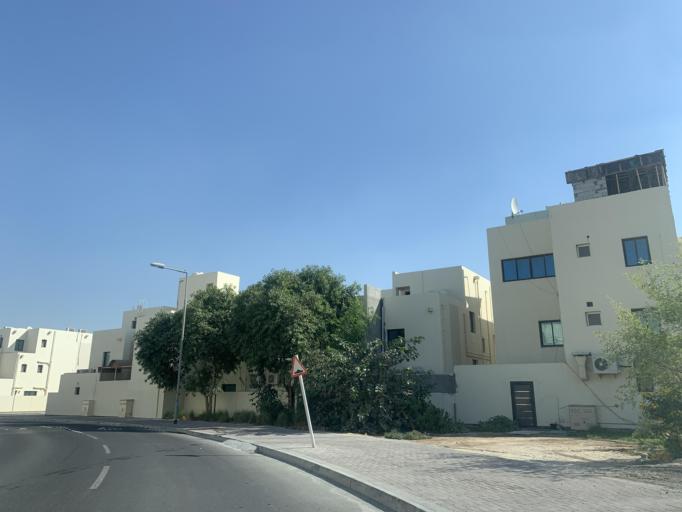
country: BH
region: Central Governorate
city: Madinat Hamad
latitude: 26.1205
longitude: 50.4831
